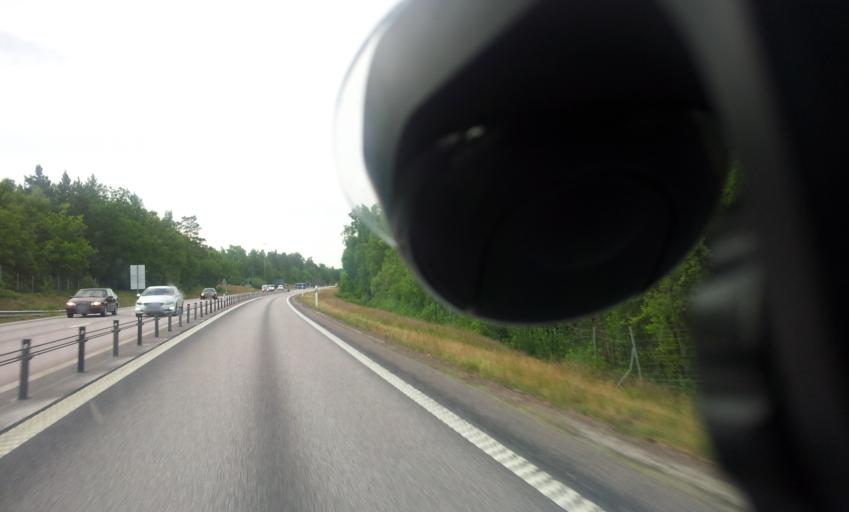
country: SE
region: Kalmar
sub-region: Oskarshamns Kommun
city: Paskallavik
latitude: 57.1817
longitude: 16.4442
